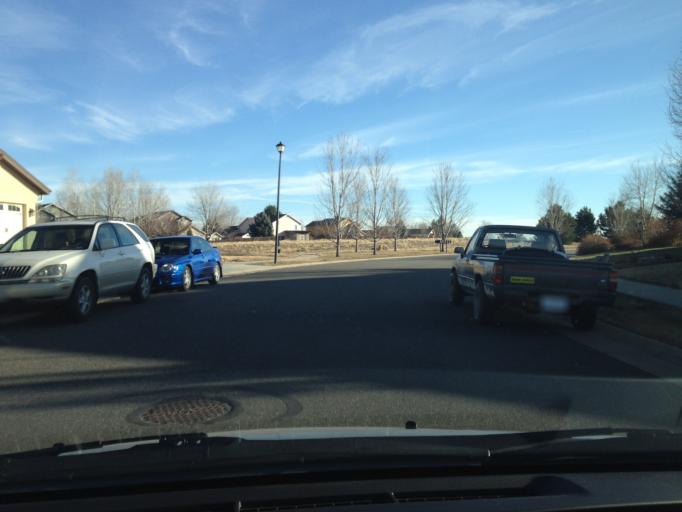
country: US
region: Colorado
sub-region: Boulder County
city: Erie
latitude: 40.0432
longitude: -105.0804
